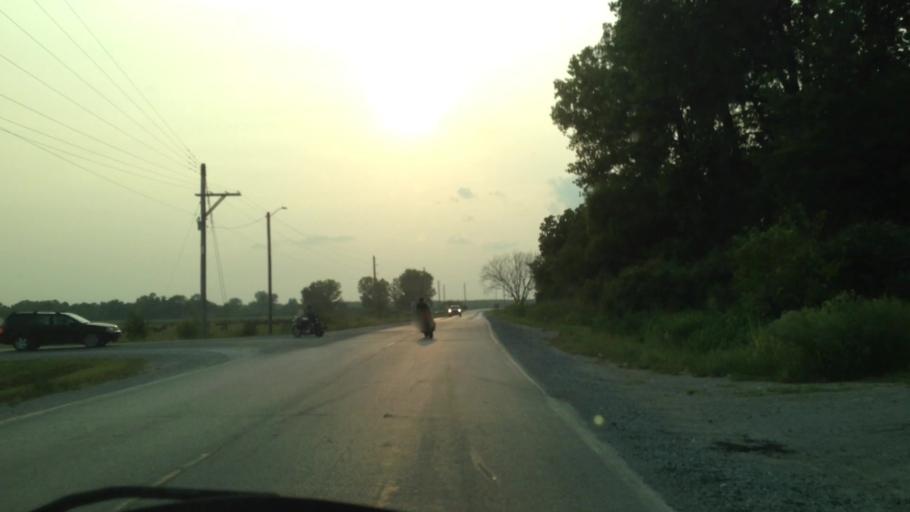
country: US
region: Iowa
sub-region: Iowa County
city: Marengo
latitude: 41.8232
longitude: -92.0639
